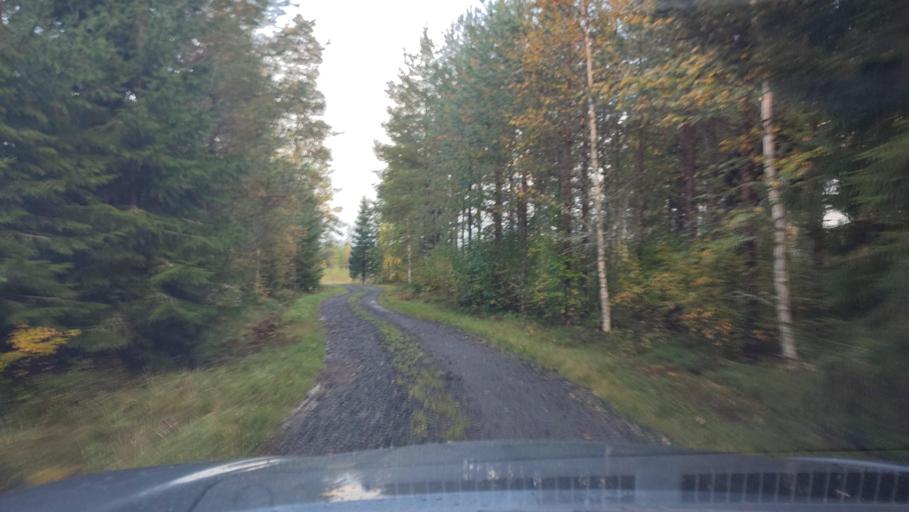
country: FI
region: Ostrobothnia
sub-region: Sydosterbotten
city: Kristinestad
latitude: 62.3023
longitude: 21.5072
